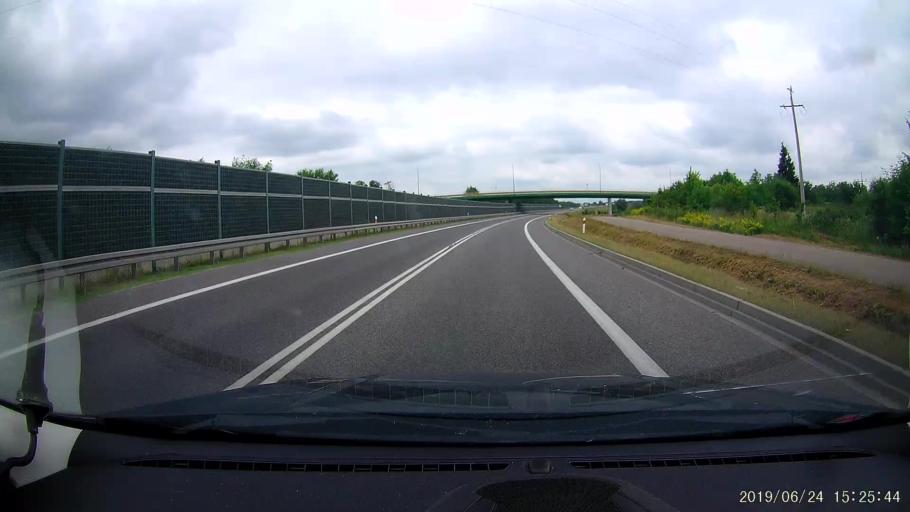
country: PL
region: Subcarpathian Voivodeship
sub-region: Powiat jaroslawski
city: Jaroslaw
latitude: 50.0319
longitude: 22.6824
